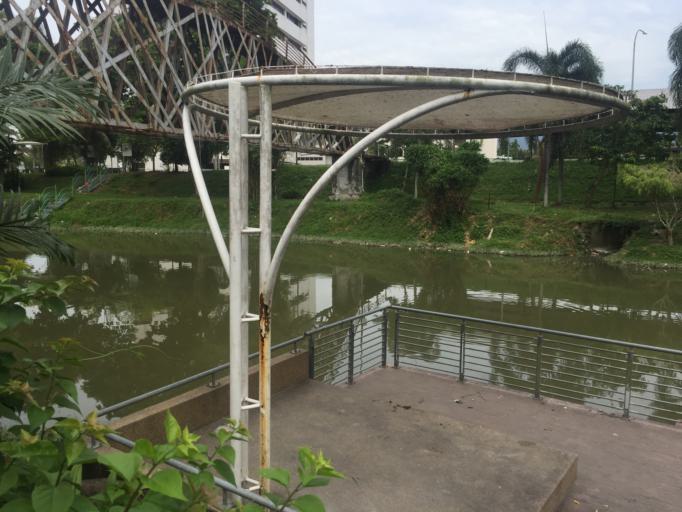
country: MY
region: Perak
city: Ipoh
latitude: 4.6001
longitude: 101.0790
